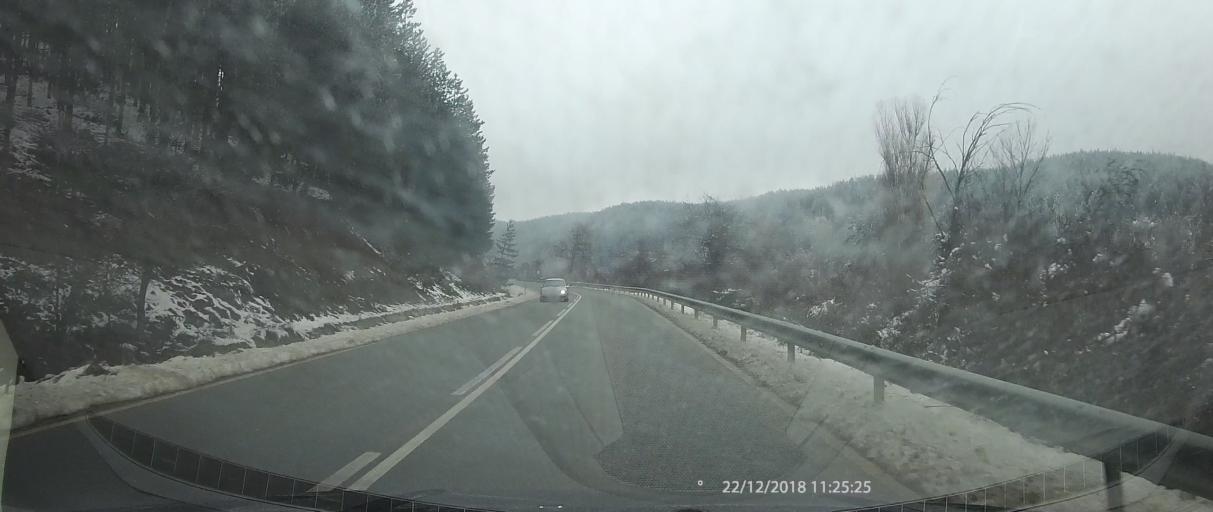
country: BG
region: Kyustendil
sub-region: Obshtina Boboshevo
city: Boboshevo
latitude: 42.2523
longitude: 22.9108
